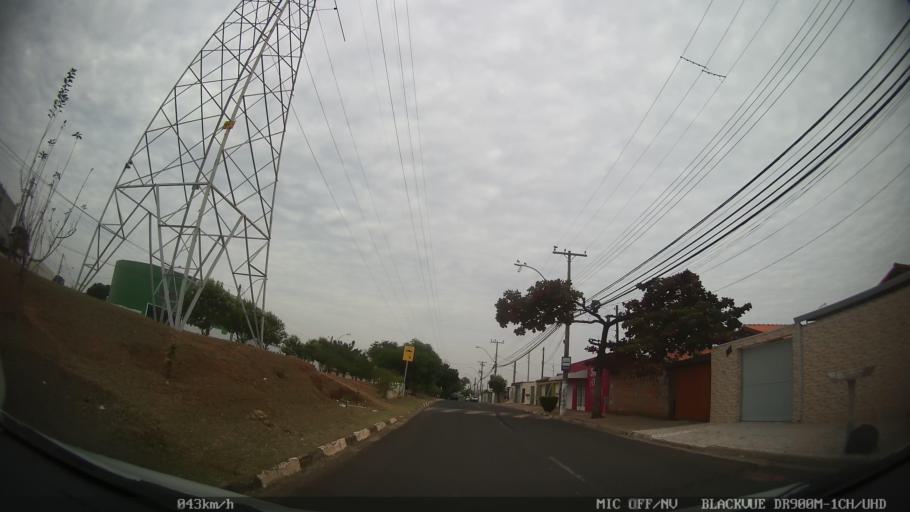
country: BR
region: Sao Paulo
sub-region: Paulinia
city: Paulinia
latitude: -22.7386
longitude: -47.1797
